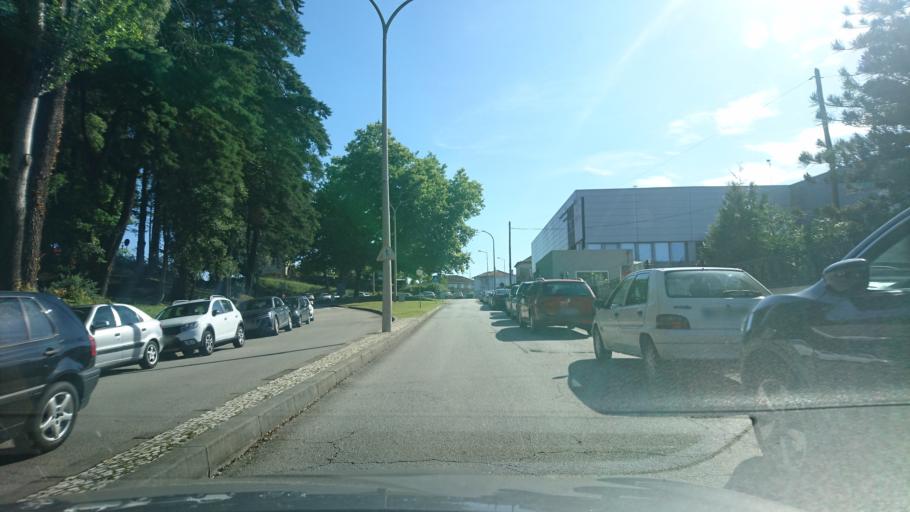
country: PT
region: Aveiro
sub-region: Sao Joao da Madeira
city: Sao Joao da Madeira
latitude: 40.8875
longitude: -8.4847
